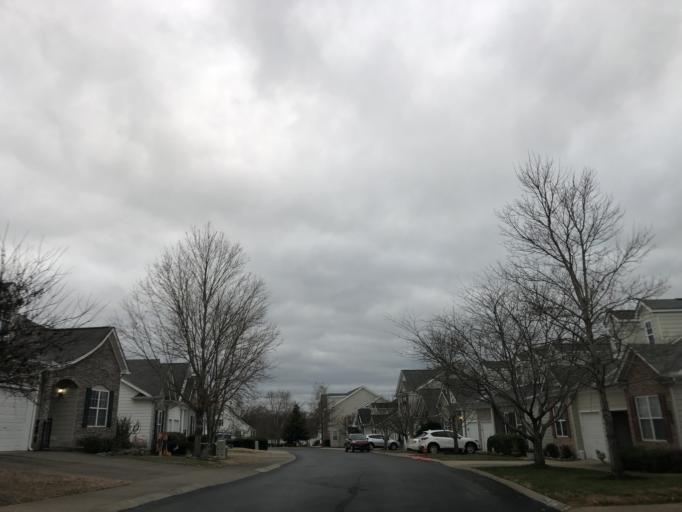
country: US
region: Tennessee
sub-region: Davidson County
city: Goodlettsville
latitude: 36.2949
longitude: -86.6870
